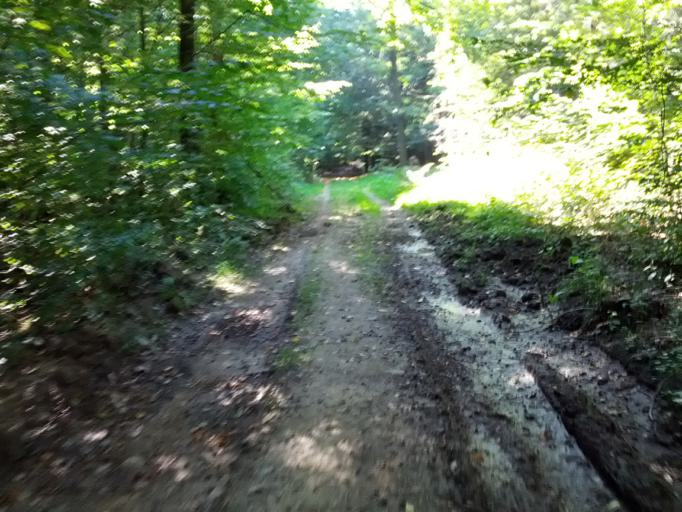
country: DE
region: Thuringia
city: Krauthausen
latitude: 51.0009
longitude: 10.2914
